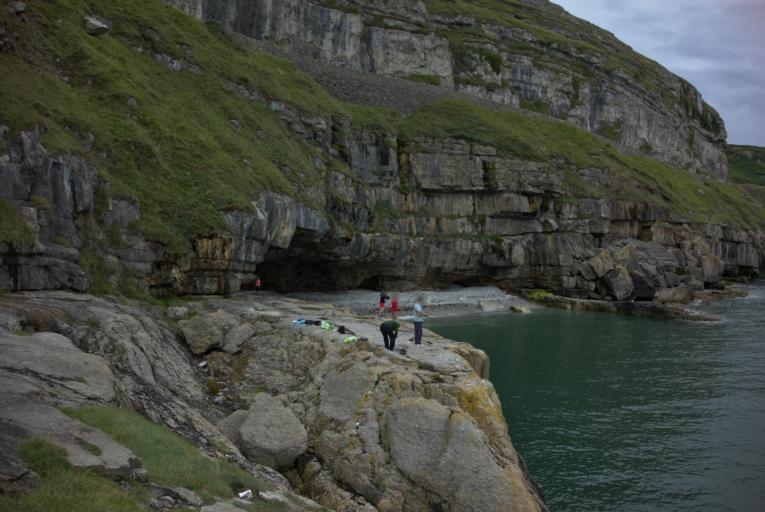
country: GB
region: Wales
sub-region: Conwy
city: Llandudno
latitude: 53.3378
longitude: -3.8353
